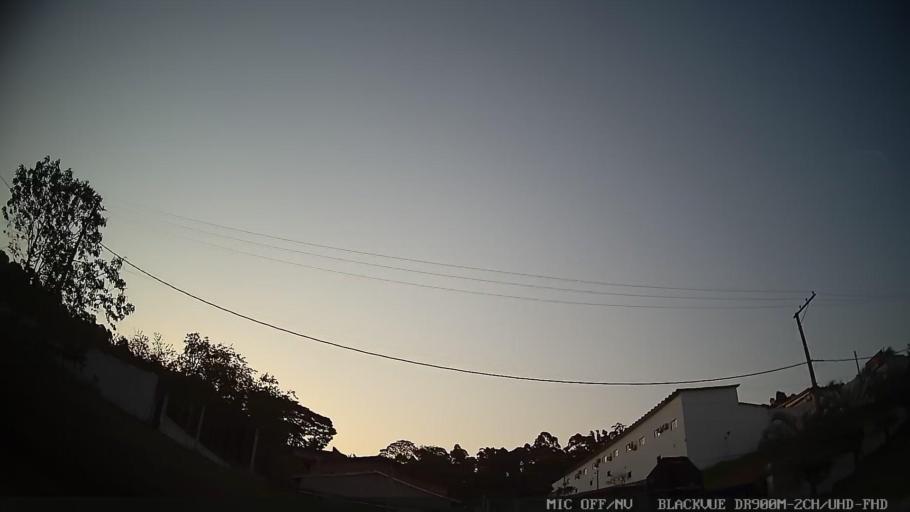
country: BR
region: Sao Paulo
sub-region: Jundiai
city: Jundiai
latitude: -23.1075
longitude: -46.8490
